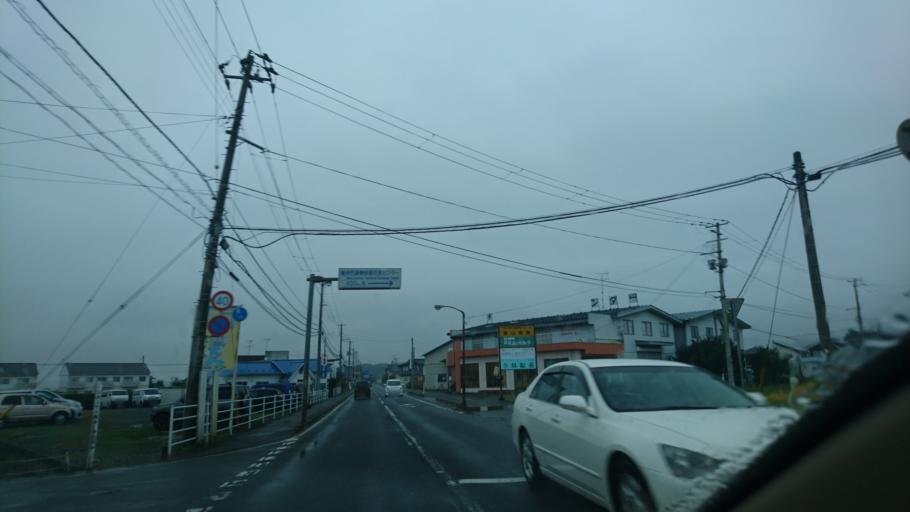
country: JP
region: Iwate
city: Mizusawa
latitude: 39.1394
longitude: 141.1796
